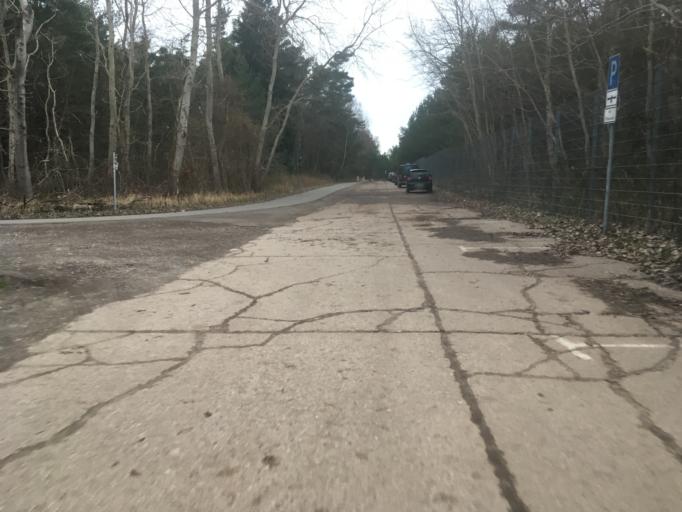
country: DE
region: Mecklenburg-Vorpommern
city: Sagard
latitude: 54.4565
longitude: 13.5675
